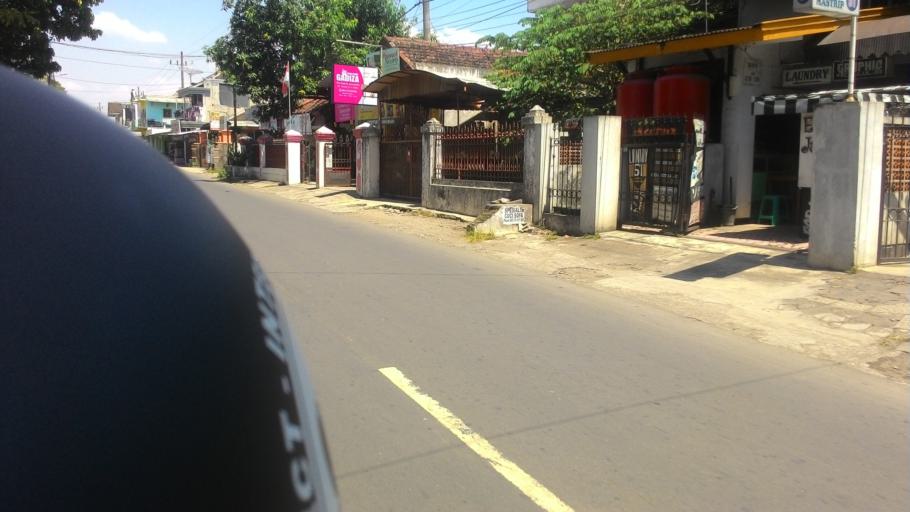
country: ID
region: East Java
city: Tegalgede Kulon
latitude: -8.1593
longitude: 113.7176
